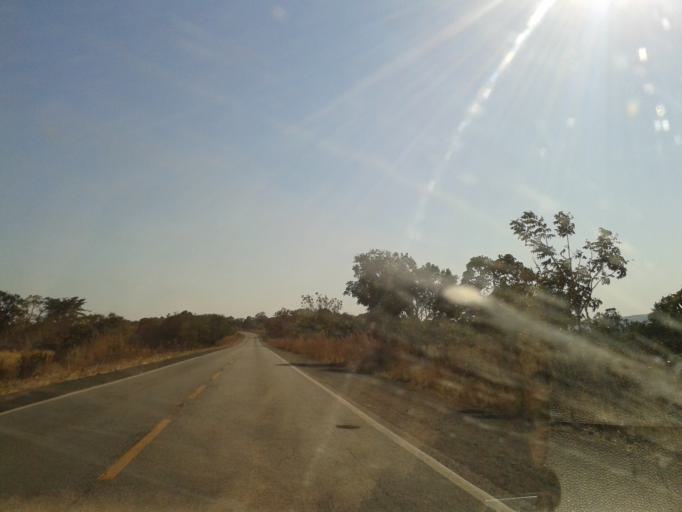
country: BR
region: Goias
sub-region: Mozarlandia
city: Mozarlandia
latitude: -14.9130
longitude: -50.5505
